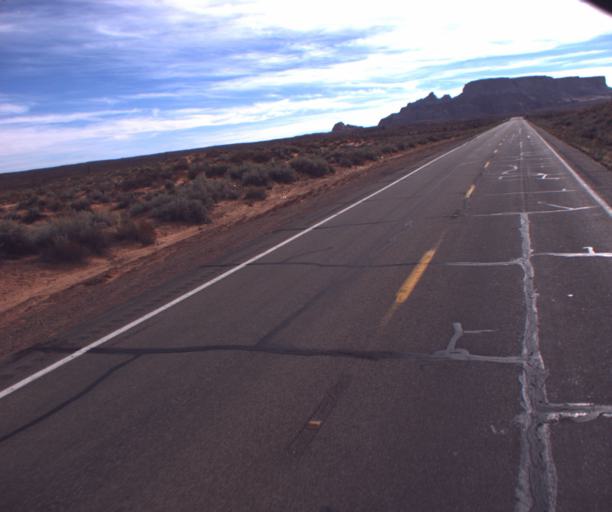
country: US
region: Arizona
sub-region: Coconino County
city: LeChee
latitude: 36.8829
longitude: -111.3536
